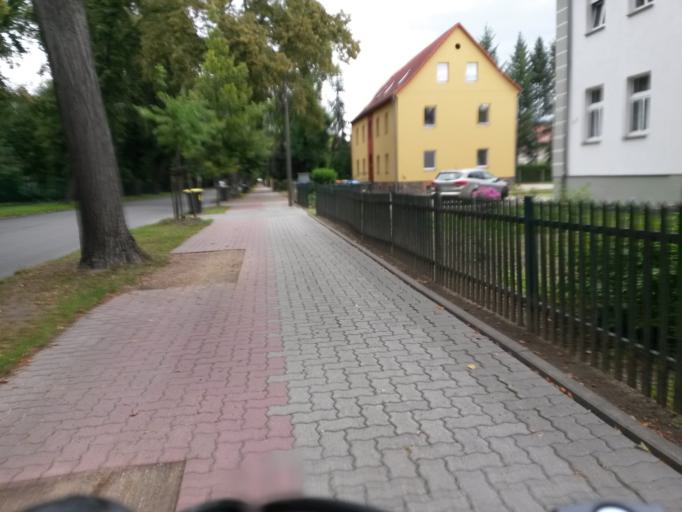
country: DE
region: Brandenburg
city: Angermunde
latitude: 53.0064
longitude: 13.9904
